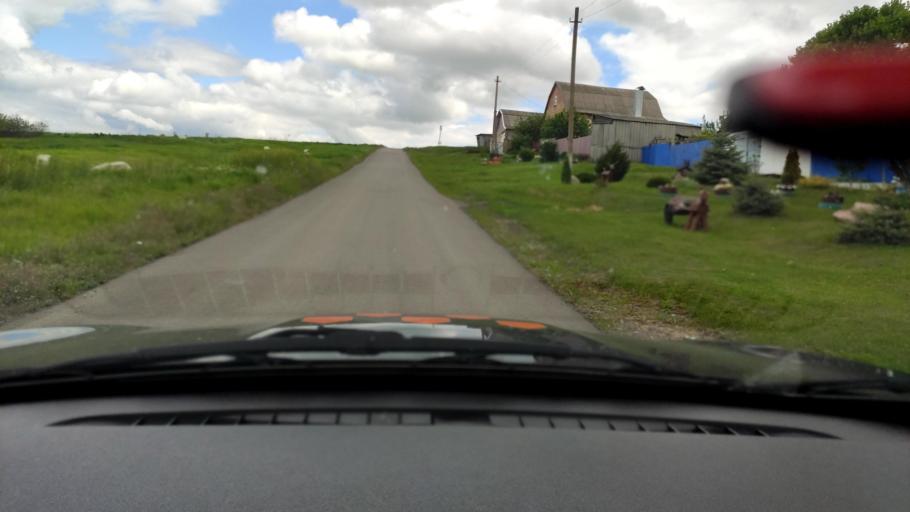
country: RU
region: Voronezj
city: Uryv-Pokrovka
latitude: 51.1068
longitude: 39.1661
